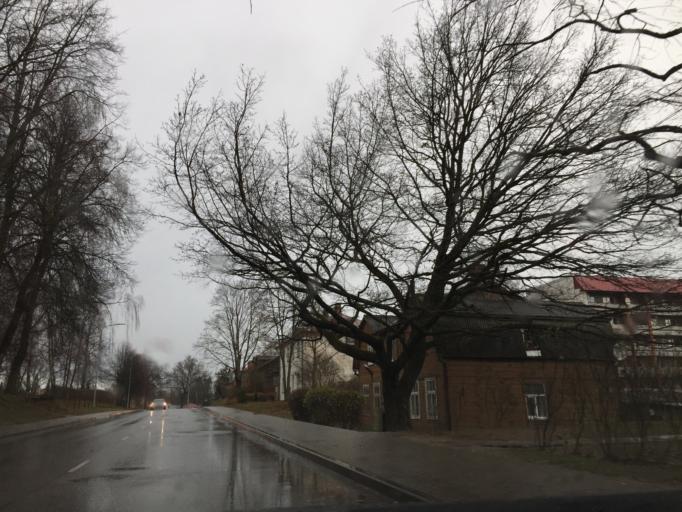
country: LV
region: Valmieras Rajons
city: Valmiera
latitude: 57.5307
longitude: 25.4236
